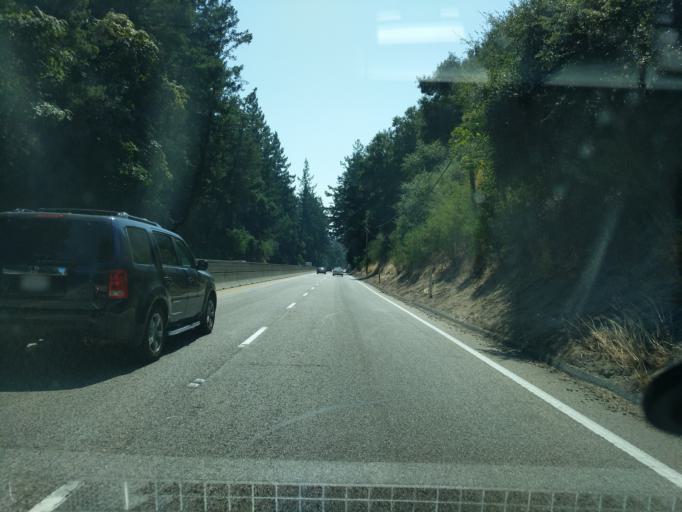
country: US
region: California
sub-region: Santa Cruz County
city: Scotts Valley
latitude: 37.0730
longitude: -121.9902
